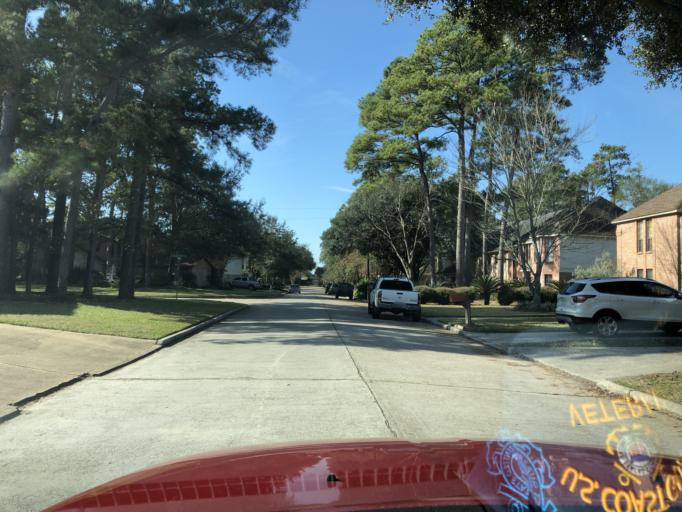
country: US
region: Texas
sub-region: Harris County
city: Tomball
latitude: 30.0304
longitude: -95.5540
